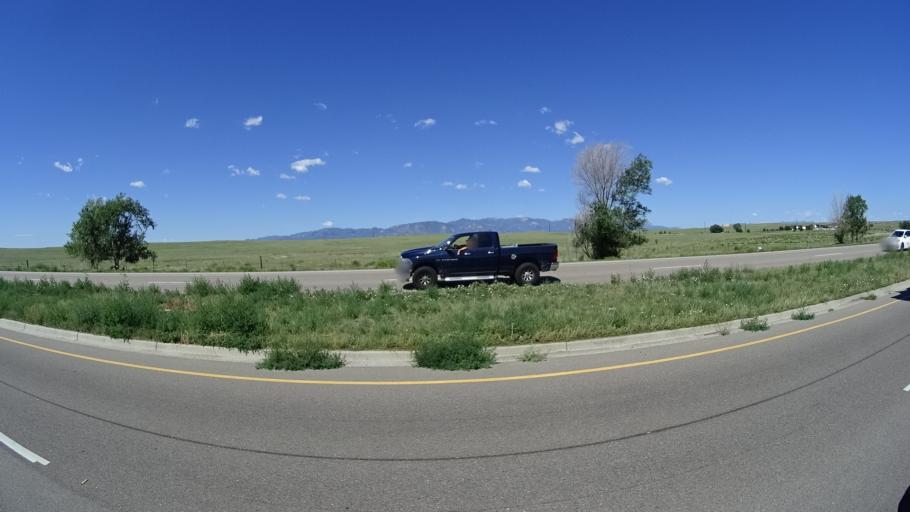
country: US
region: Colorado
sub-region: El Paso County
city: Security-Widefield
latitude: 38.7580
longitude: -104.6597
